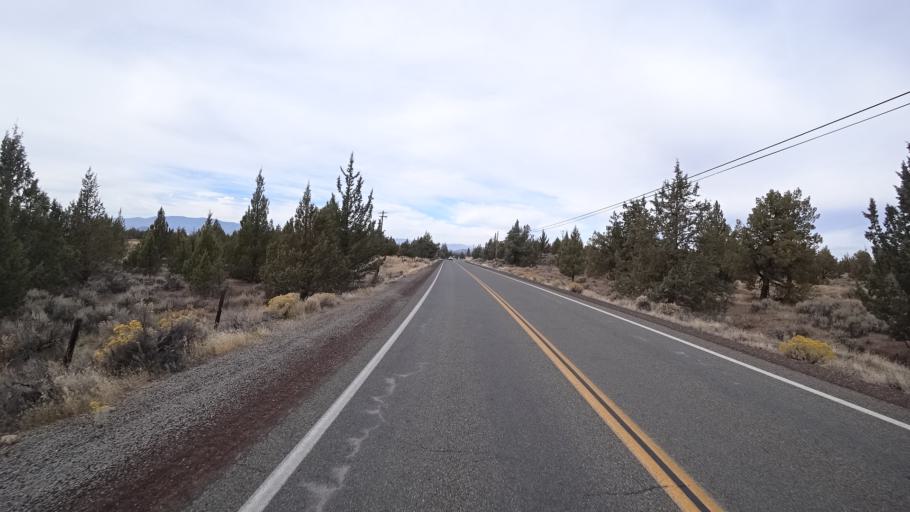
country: US
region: California
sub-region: Siskiyou County
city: Montague
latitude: 41.6160
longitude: -122.3704
